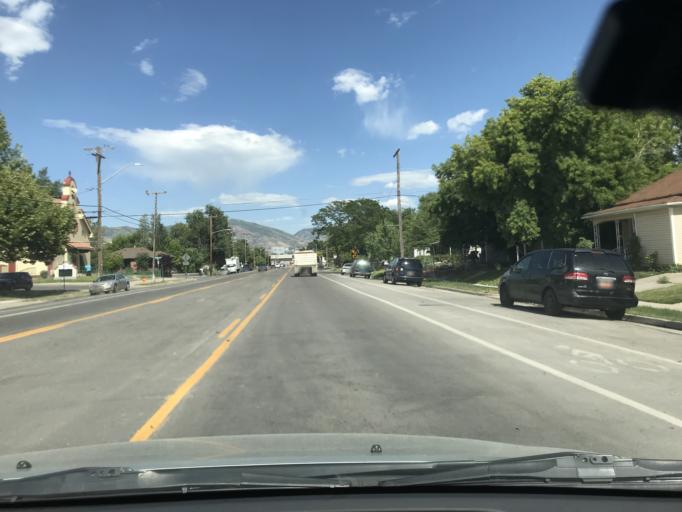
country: US
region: Utah
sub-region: Salt Lake County
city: Salt Lake City
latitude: 40.7607
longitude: -111.9221
